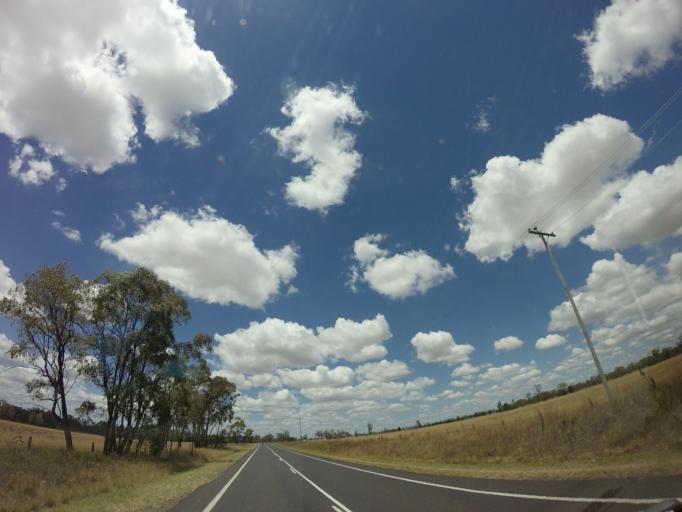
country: AU
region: Queensland
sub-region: Toowoomba
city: Oakey
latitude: -27.8773
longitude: 151.2328
